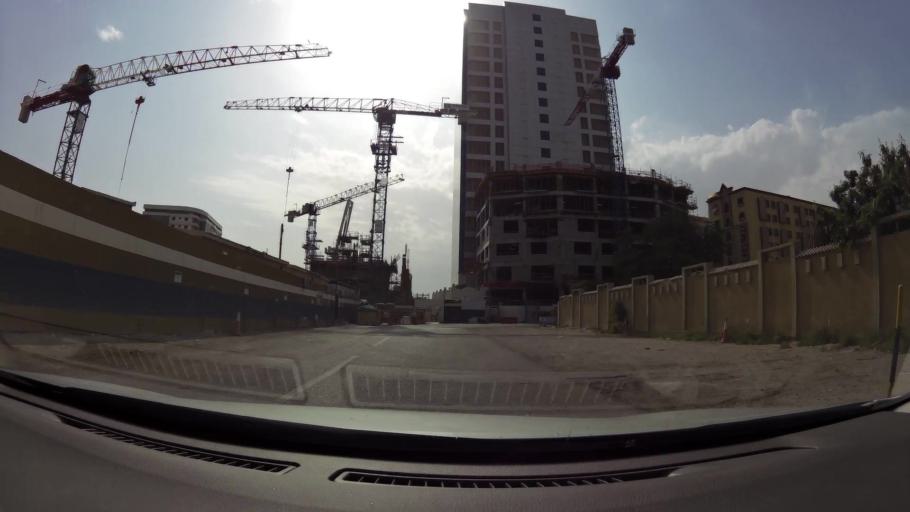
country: QA
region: Baladiyat ad Dawhah
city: Doha
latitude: 25.2749
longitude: 51.5107
